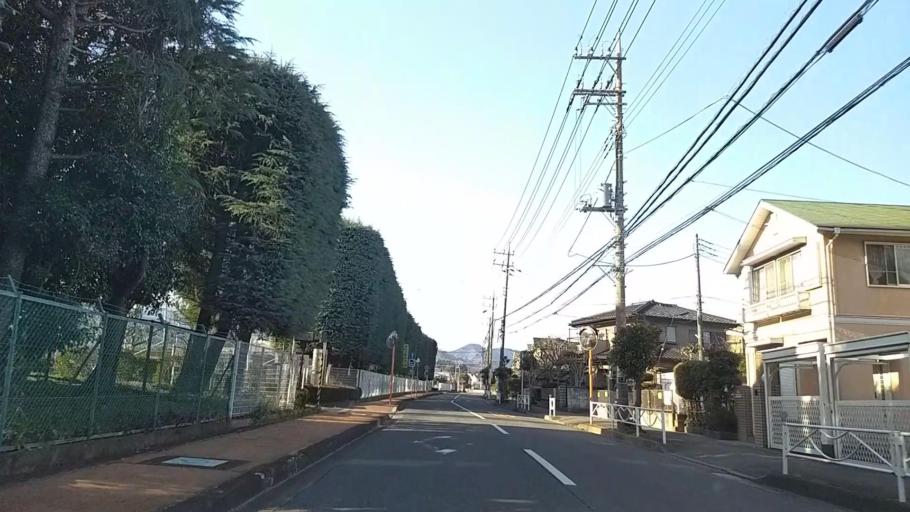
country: JP
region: Kanagawa
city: Atsugi
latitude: 35.4607
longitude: 139.3306
